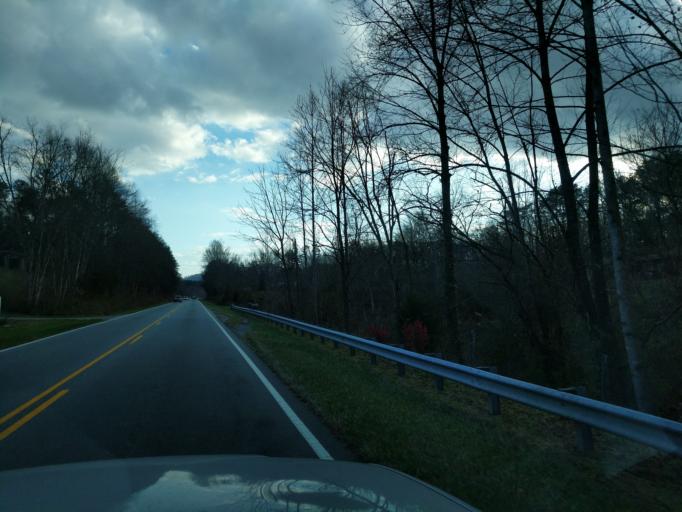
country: US
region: North Carolina
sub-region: McDowell County
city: West Marion
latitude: 35.5967
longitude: -81.9839
